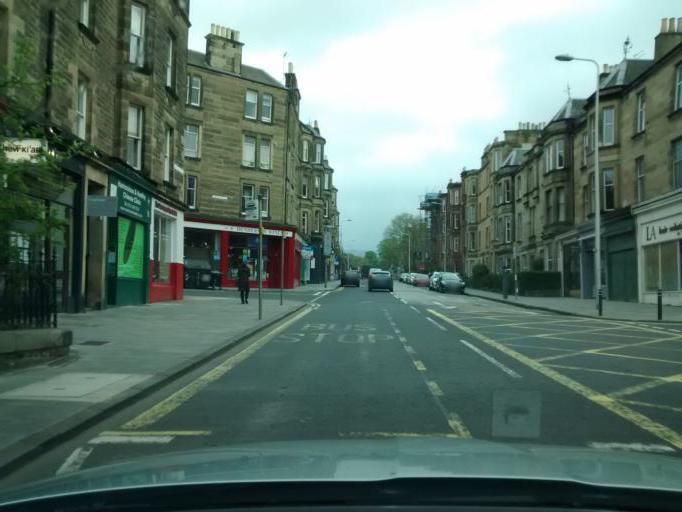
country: GB
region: Scotland
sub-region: Edinburgh
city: Edinburgh
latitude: 55.9226
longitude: -3.2109
